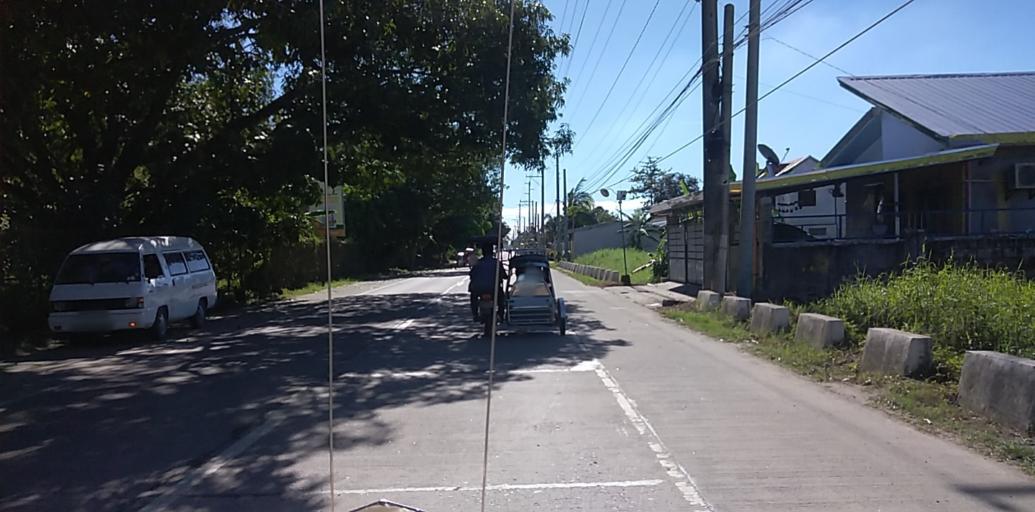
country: PH
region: Central Luzon
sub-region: Province of Pampanga
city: Santo Domingo
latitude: 15.0638
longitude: 120.7698
